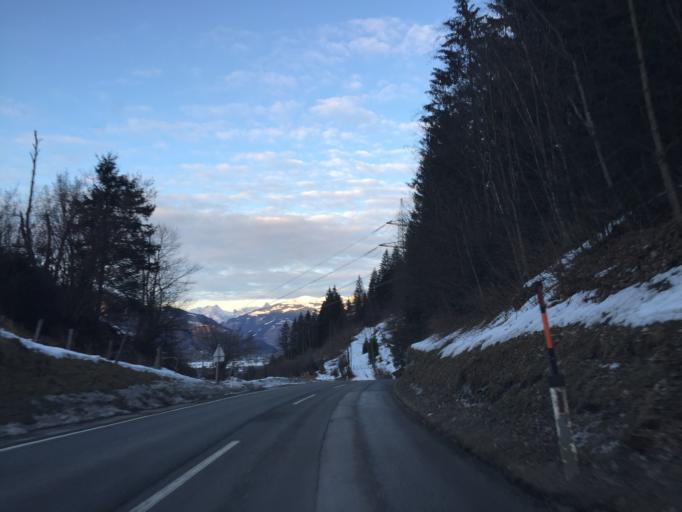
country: AT
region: Salzburg
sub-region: Politischer Bezirk Zell am See
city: Kaprun
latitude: 47.2551
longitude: 12.7436
